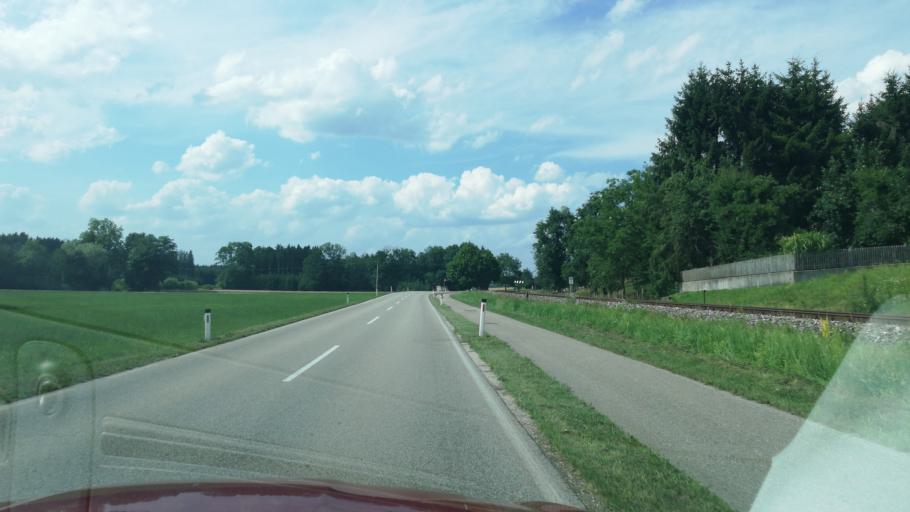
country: AT
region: Upper Austria
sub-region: Politischer Bezirk Vocklabruck
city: Puhret
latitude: 48.0282
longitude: 13.7048
